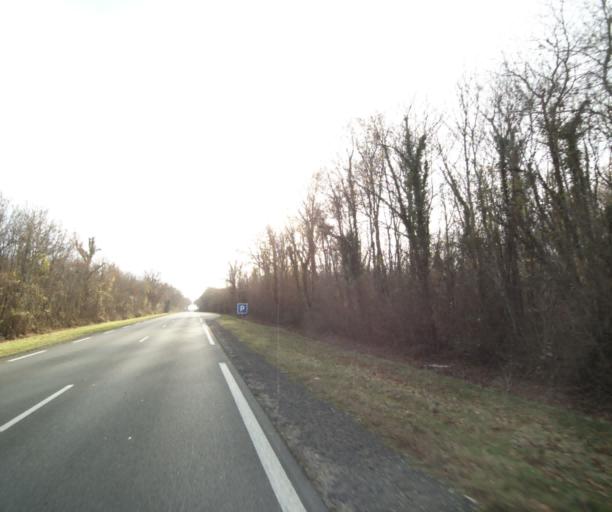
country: FR
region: Poitou-Charentes
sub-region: Departement de la Charente-Maritime
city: Saint-Hilaire-de-Villefranche
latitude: 45.8243
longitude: -0.5430
